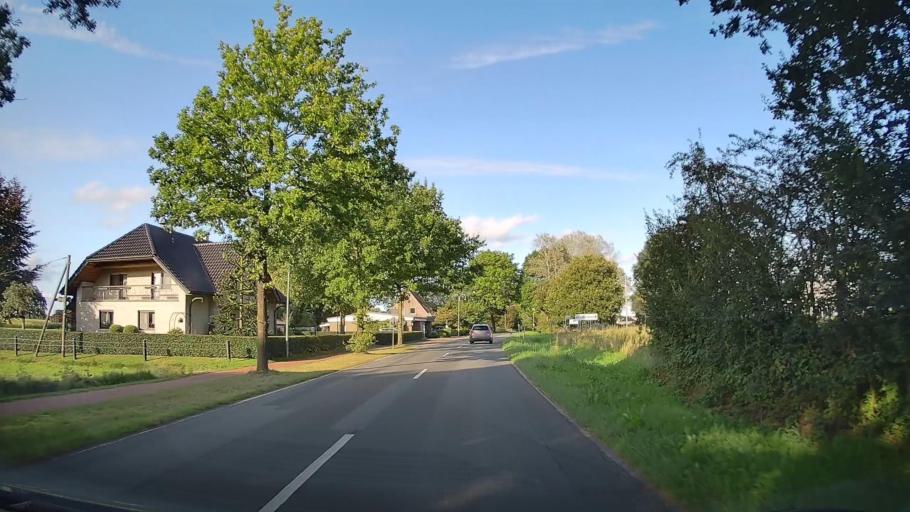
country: DE
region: Lower Saxony
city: Ostrhauderfehn
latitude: 53.1298
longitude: 7.6782
